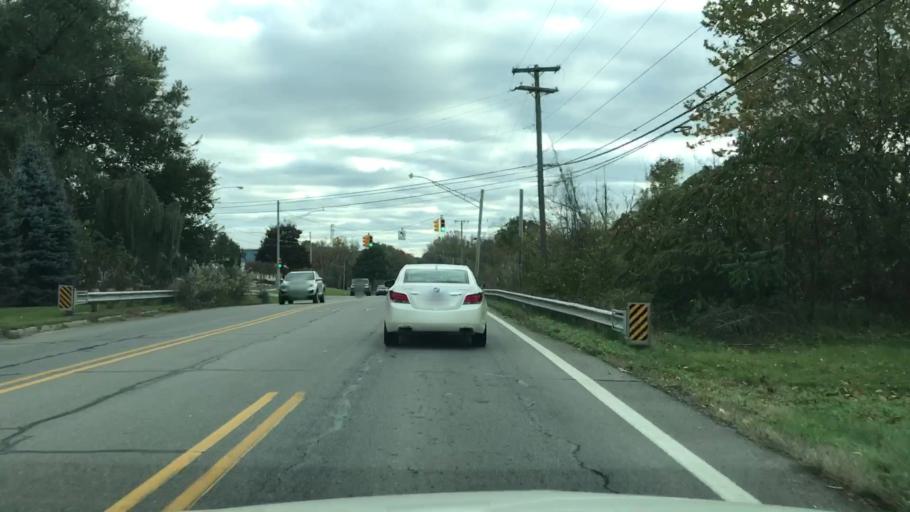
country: US
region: Michigan
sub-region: Macomb County
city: Shelby
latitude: 42.6618
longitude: -83.0735
